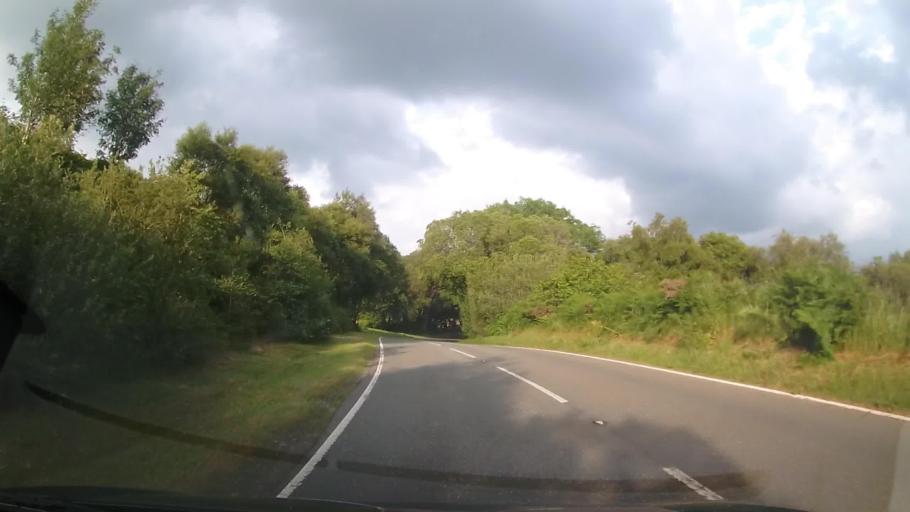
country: GB
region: Wales
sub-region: Denbighshire
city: Llandrillo
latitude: 52.9029
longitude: -3.5088
